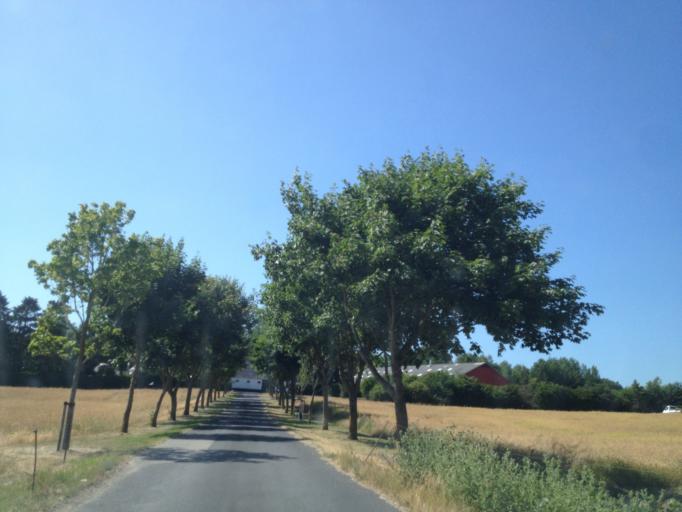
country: DK
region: Capital Region
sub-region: Fredensborg Kommune
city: Niva
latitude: 55.9620
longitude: 12.4900
